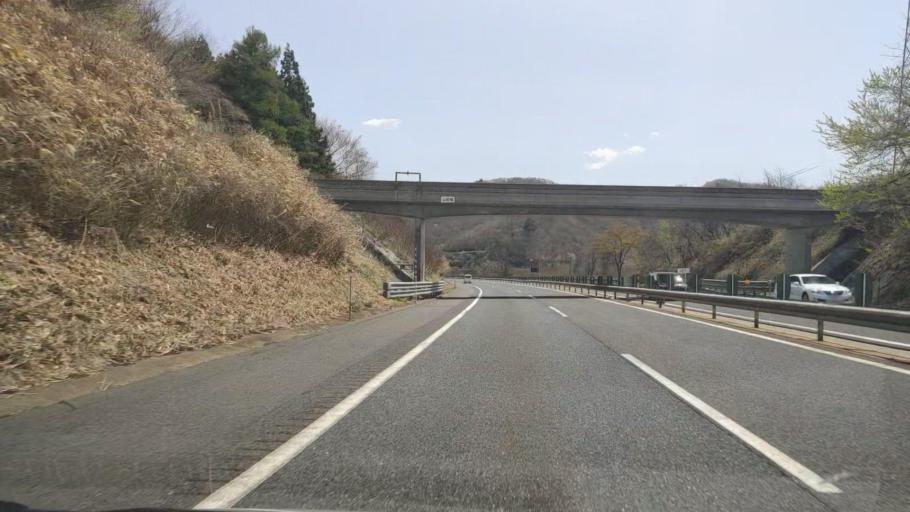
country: JP
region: Iwate
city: Ichinohe
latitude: 40.2195
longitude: 141.2425
